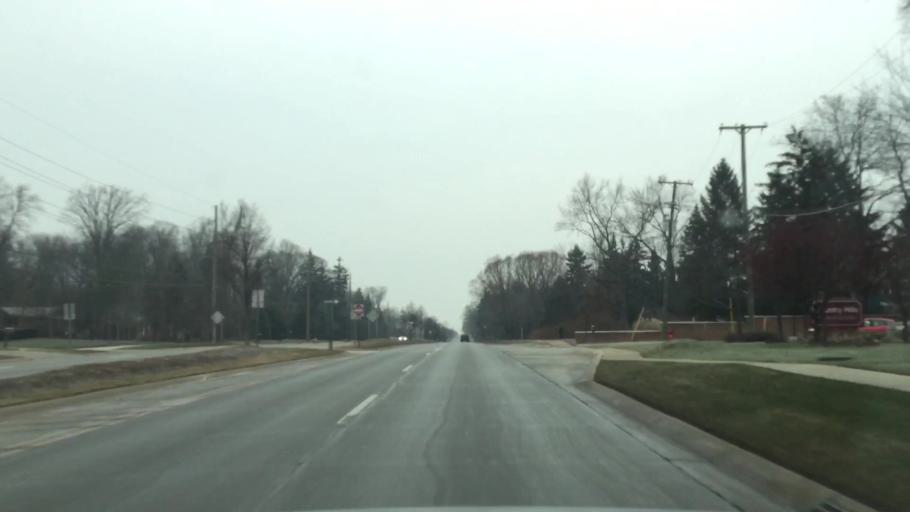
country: US
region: Michigan
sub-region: Oakland County
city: Farmington
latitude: 42.4733
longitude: -83.3574
